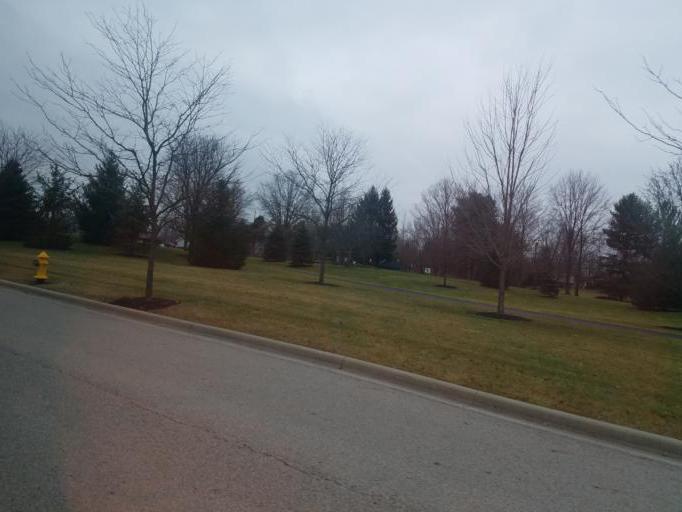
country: US
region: Ohio
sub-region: Franklin County
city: Westerville
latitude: 40.1908
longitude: -82.9260
